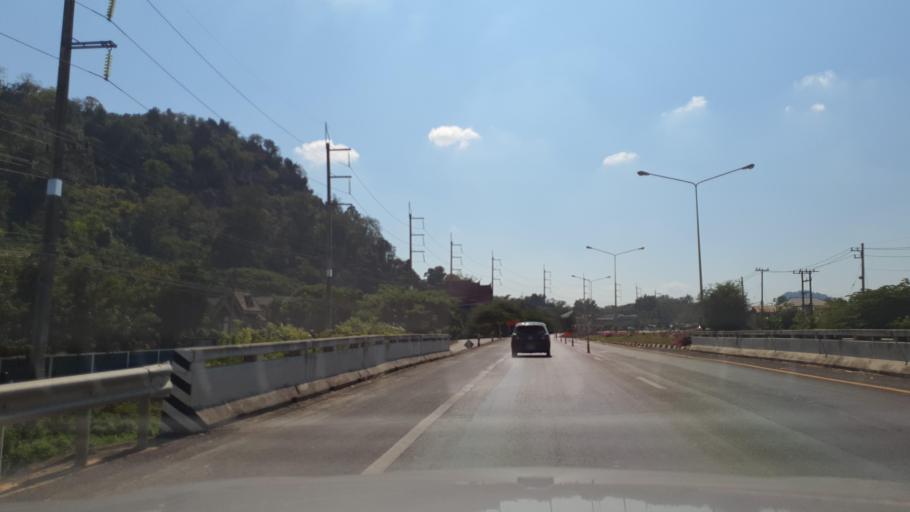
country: TH
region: Nan
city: Nan
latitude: 18.8869
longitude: 100.7506
